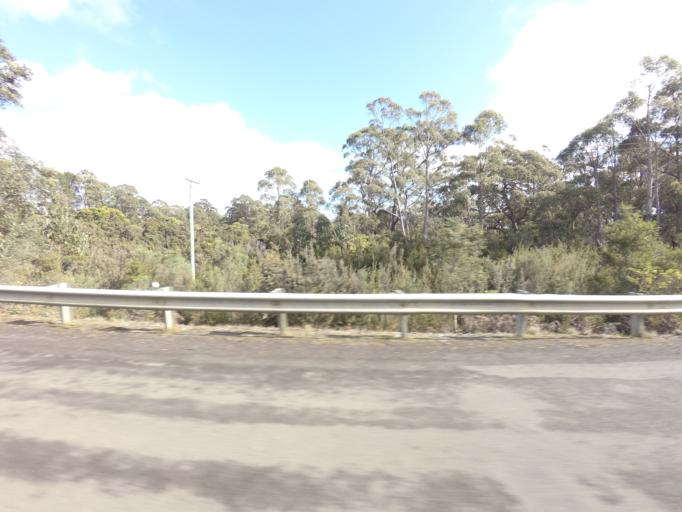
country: AU
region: Tasmania
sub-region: Huon Valley
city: Geeveston
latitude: -43.4207
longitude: 146.9069
